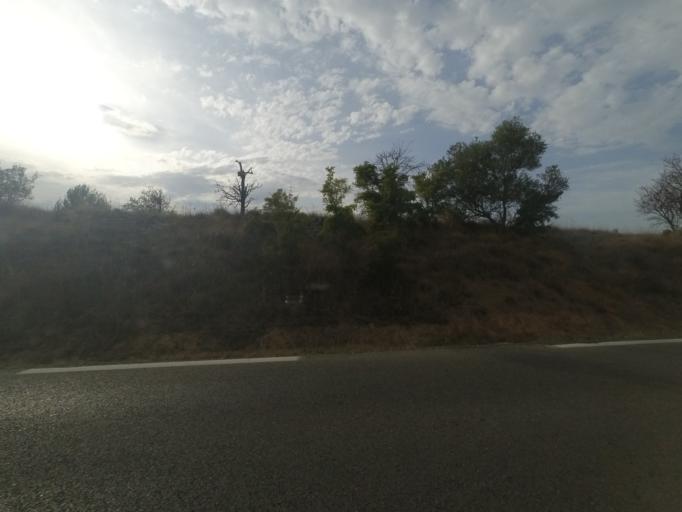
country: FR
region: Languedoc-Roussillon
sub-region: Departement de l'Herault
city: Restinclieres
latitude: 43.7278
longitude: 4.0423
